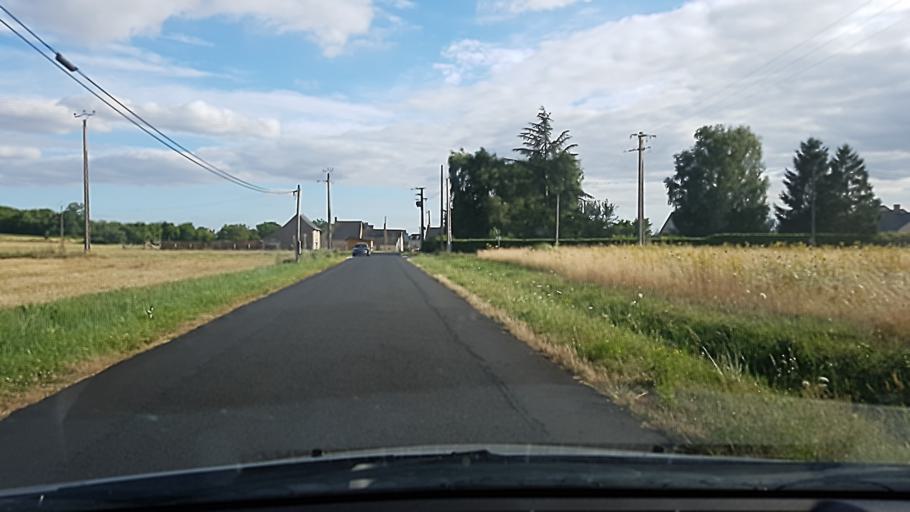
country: FR
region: Pays de la Loire
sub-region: Departement de Maine-et-Loire
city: Maze
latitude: 47.4734
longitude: -0.2823
